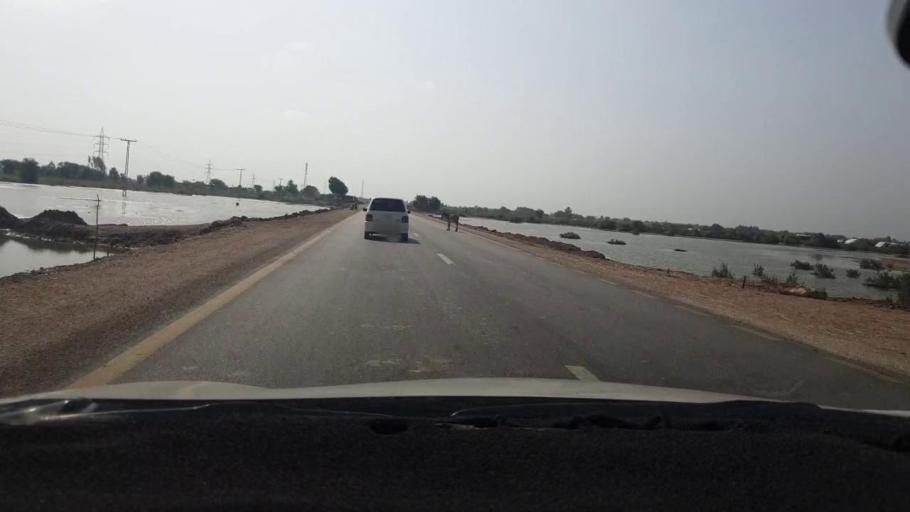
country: PK
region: Sindh
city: Jhol
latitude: 25.8922
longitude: 69.0291
